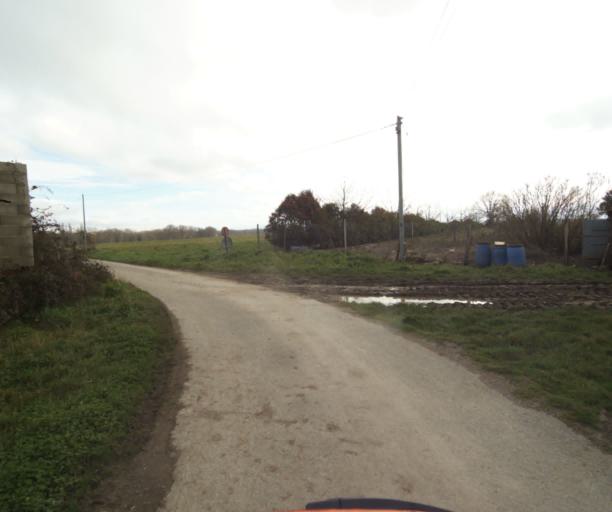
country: FR
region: Languedoc-Roussillon
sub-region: Departement de l'Aude
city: Belpech
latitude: 43.1618
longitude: 1.6958
